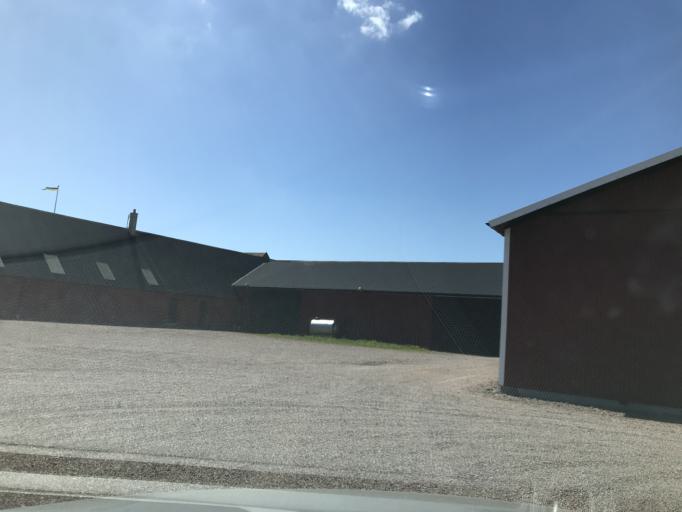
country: SE
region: Skane
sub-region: Landskrona
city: Asmundtorp
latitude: 55.9098
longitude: 12.8891
